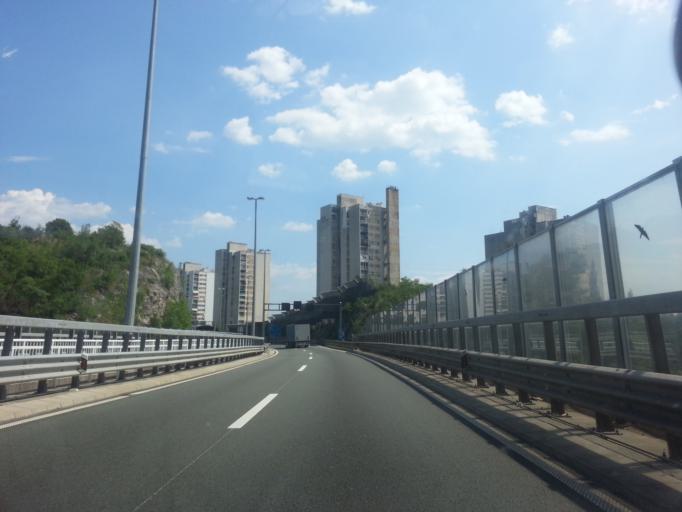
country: HR
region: Primorsko-Goranska
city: Drenova
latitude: 45.3411
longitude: 14.4308
